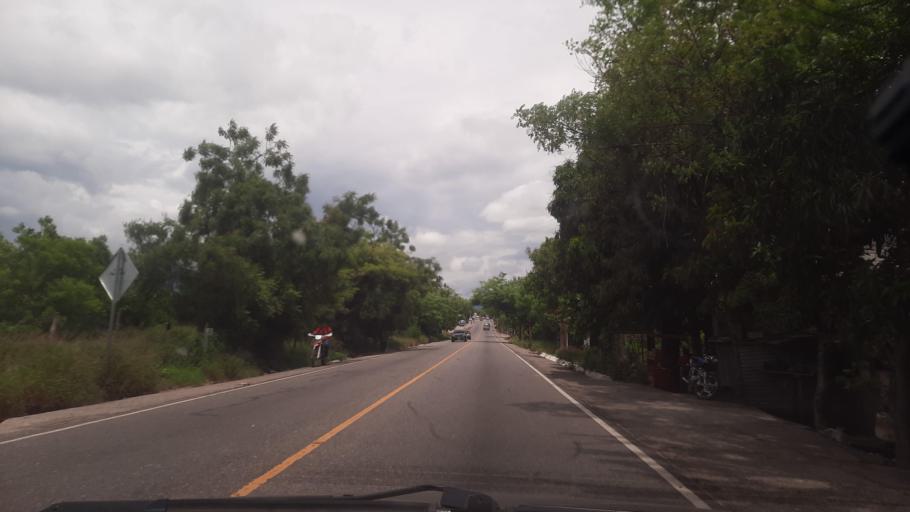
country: GT
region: Zacapa
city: Estanzuela
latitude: 15.0006
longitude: -89.5693
